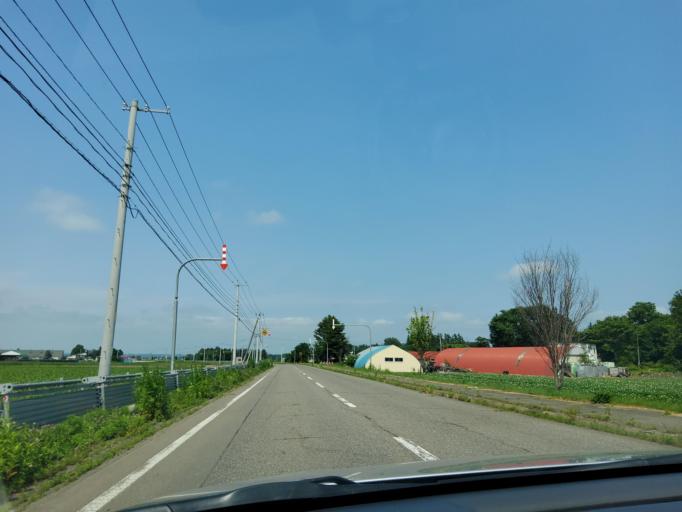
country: JP
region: Hokkaido
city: Obihiro
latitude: 42.8715
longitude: 143.0240
